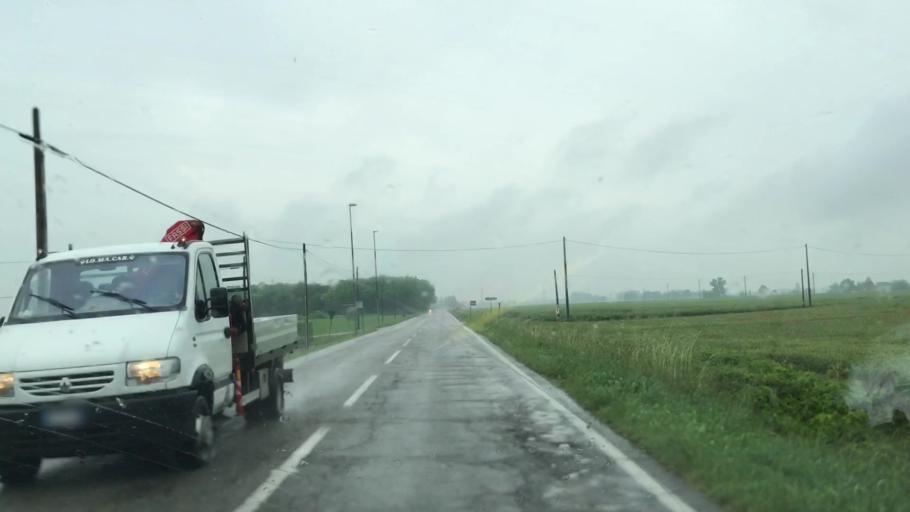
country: IT
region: Lombardy
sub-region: Provincia di Mantova
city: Gazzuolo
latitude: 45.0575
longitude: 10.5782
